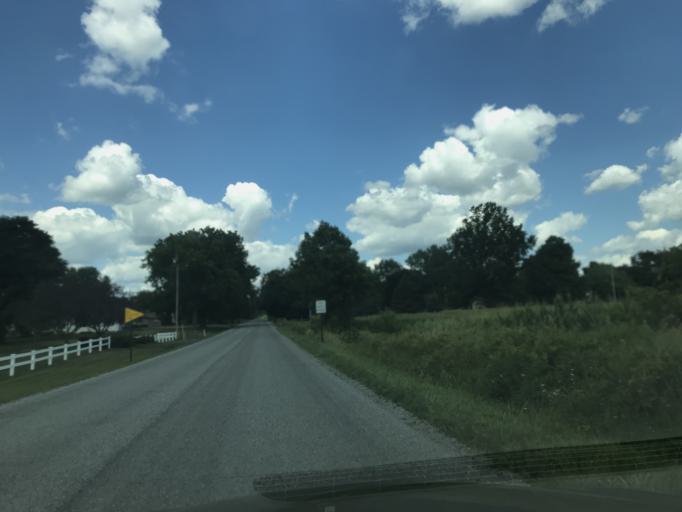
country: US
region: Michigan
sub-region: Ingham County
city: Holt
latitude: 42.6059
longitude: -84.5625
